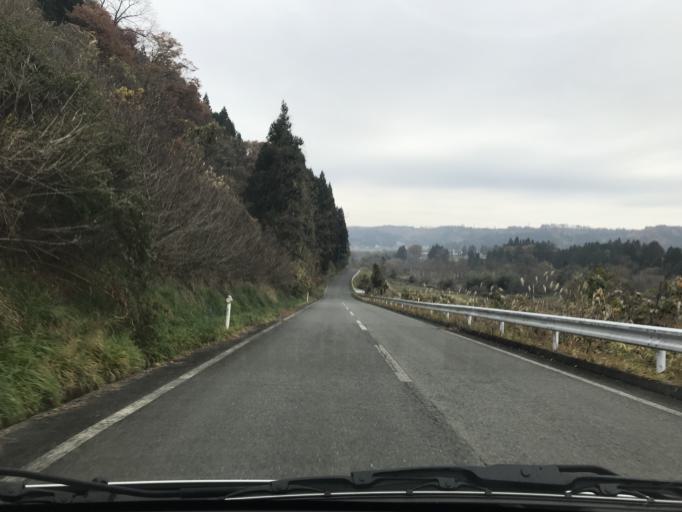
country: JP
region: Iwate
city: Ichinoseki
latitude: 39.0175
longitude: 141.0739
